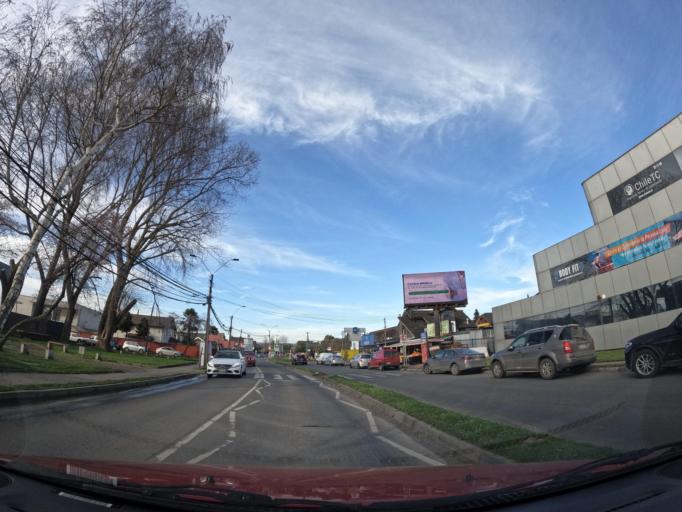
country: CL
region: Biobio
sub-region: Provincia de Concepcion
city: Concepcion
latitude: -36.7901
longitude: -73.0597
